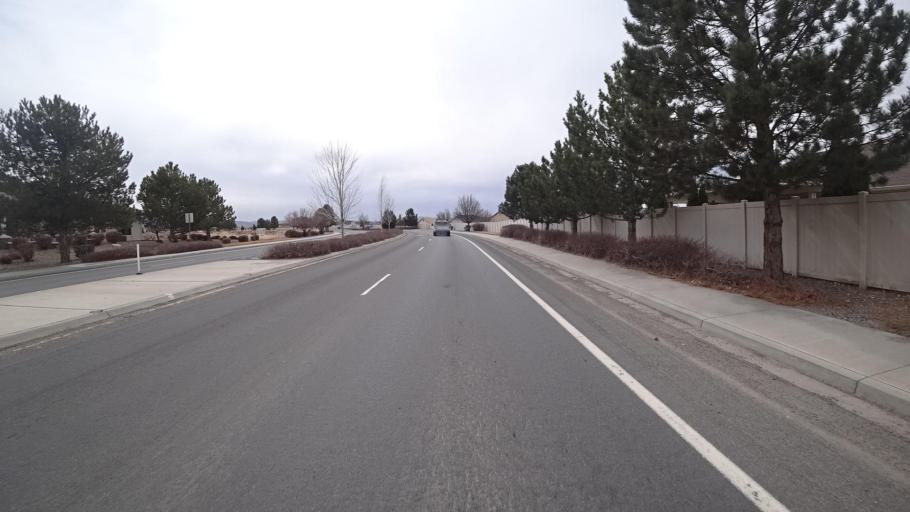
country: US
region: Nevada
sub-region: Washoe County
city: Spanish Springs
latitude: 39.6684
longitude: -119.7070
